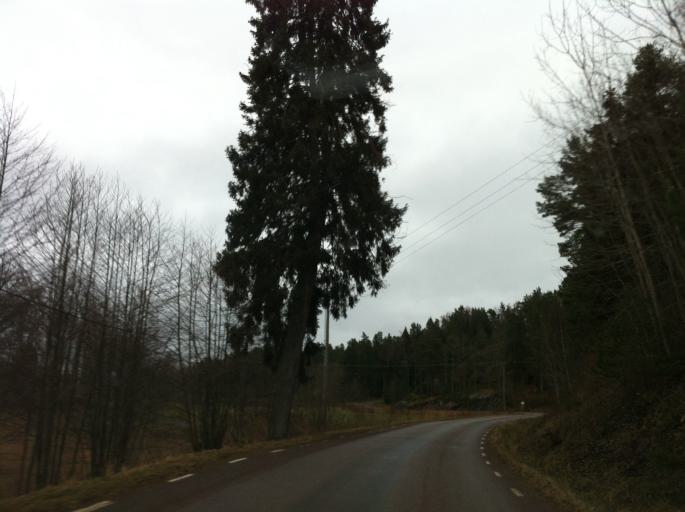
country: SE
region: Kalmar
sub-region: Vasterviks Kommun
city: Vaestervik
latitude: 57.9065
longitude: 16.6970
